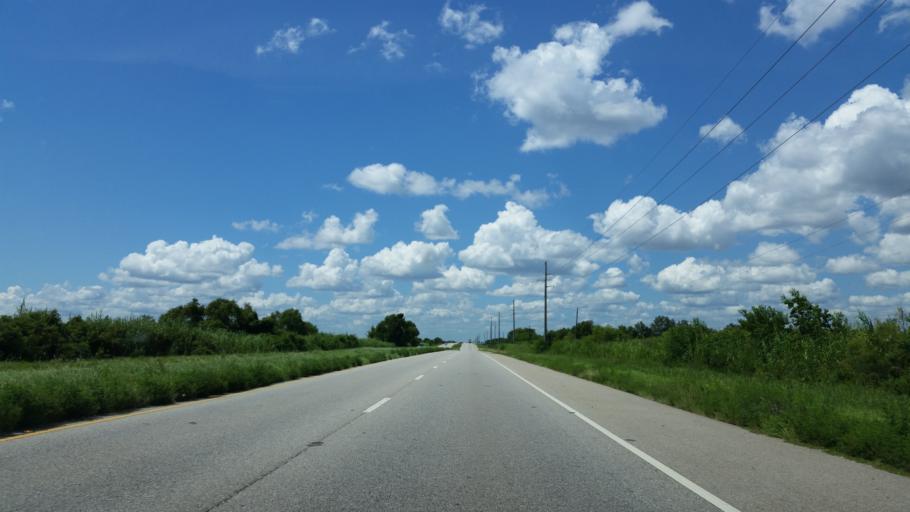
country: US
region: Alabama
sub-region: Baldwin County
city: Spanish Fort
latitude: 30.6711
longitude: -87.9437
